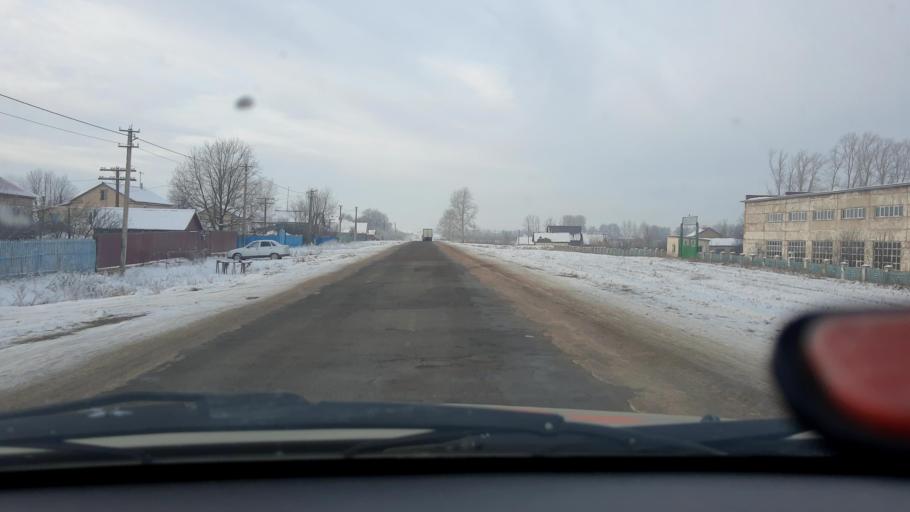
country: RU
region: Bashkortostan
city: Avdon
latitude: 54.3624
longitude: 55.8356
